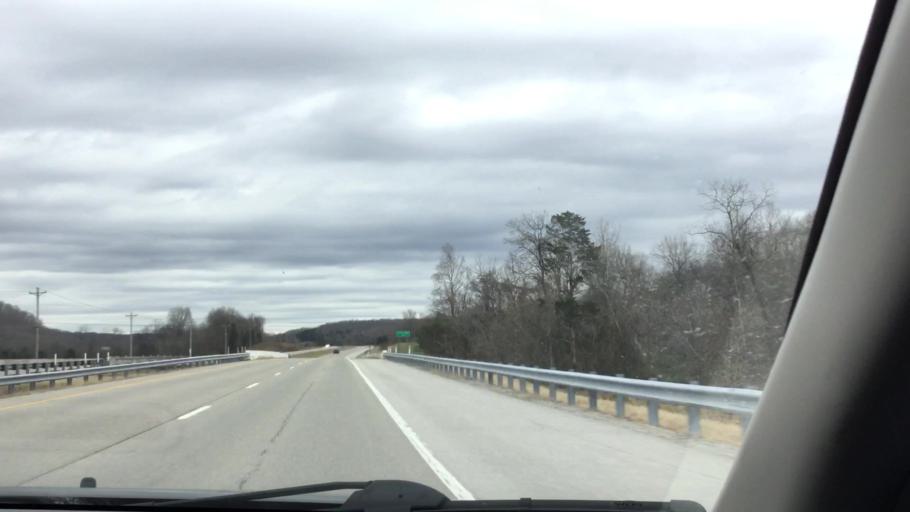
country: US
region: Tennessee
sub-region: Lewis County
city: Hohenwald
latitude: 35.5894
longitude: -87.4500
